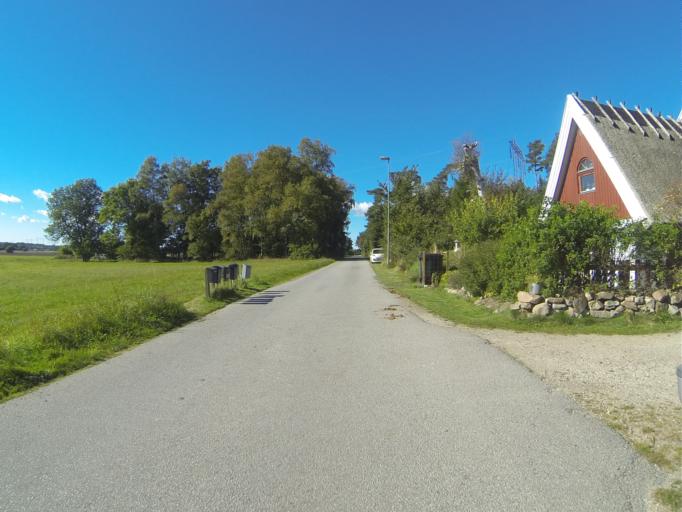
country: SE
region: Skane
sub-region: Hoors Kommun
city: Loberod
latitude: 55.7266
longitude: 13.3905
